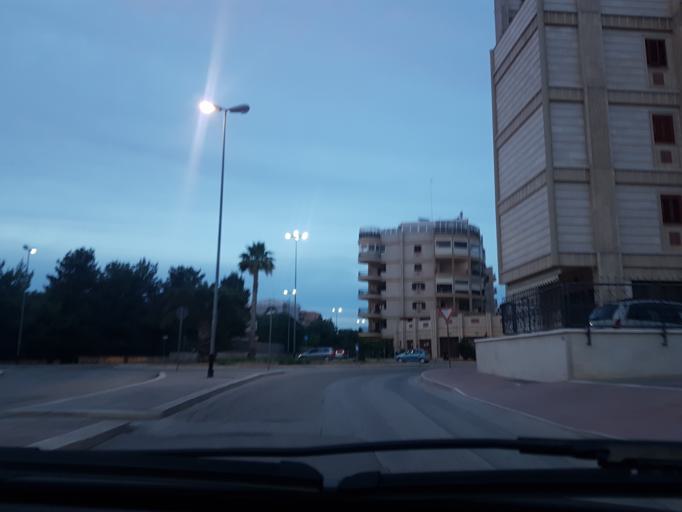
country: IT
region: Apulia
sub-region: Provincia di Barletta - Andria - Trani
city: Barletta
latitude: 41.3079
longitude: 16.2662
